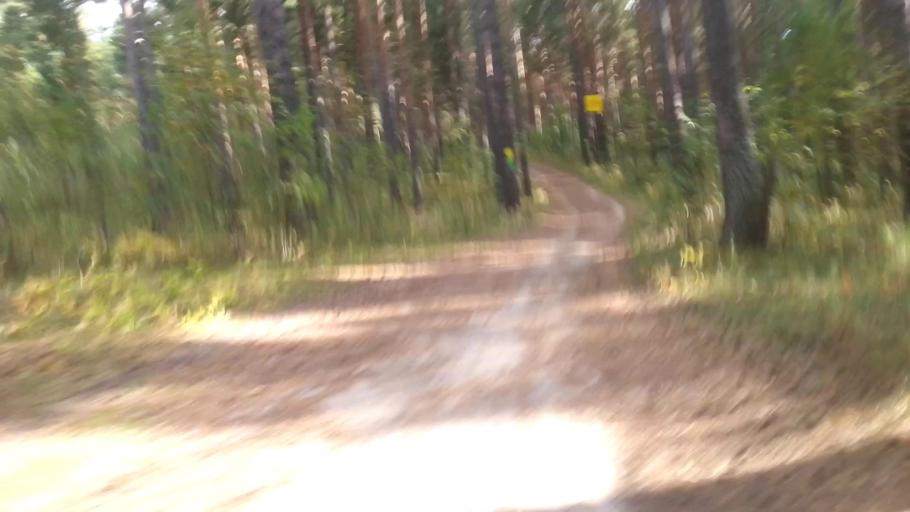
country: RU
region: Altai Krai
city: Yuzhnyy
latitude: 53.2845
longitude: 83.6990
